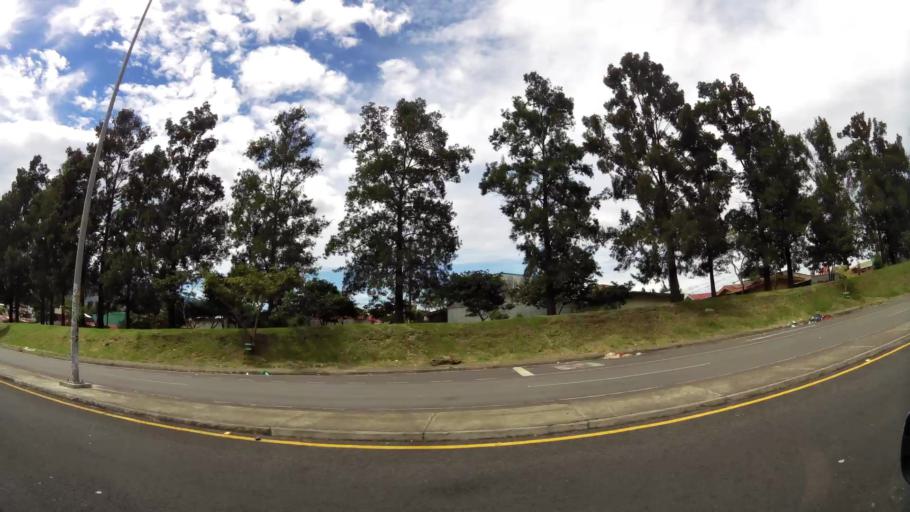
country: CR
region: San Jose
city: San Jose
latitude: 9.9092
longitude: -84.0743
